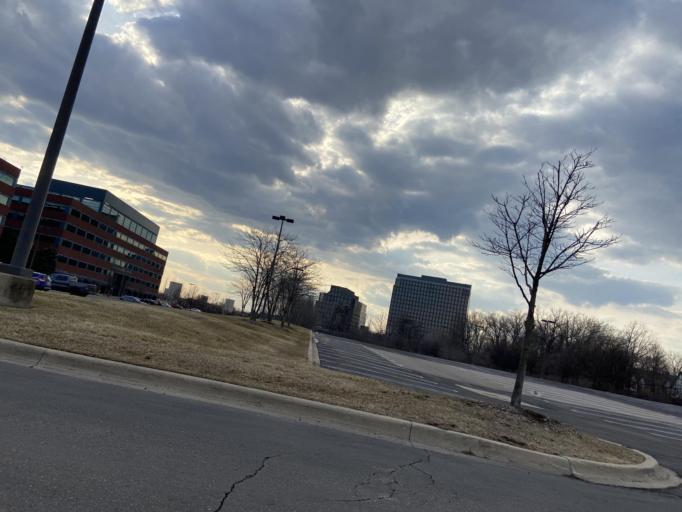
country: US
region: Michigan
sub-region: Oakland County
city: Southfield
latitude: 42.4829
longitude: -83.2480
